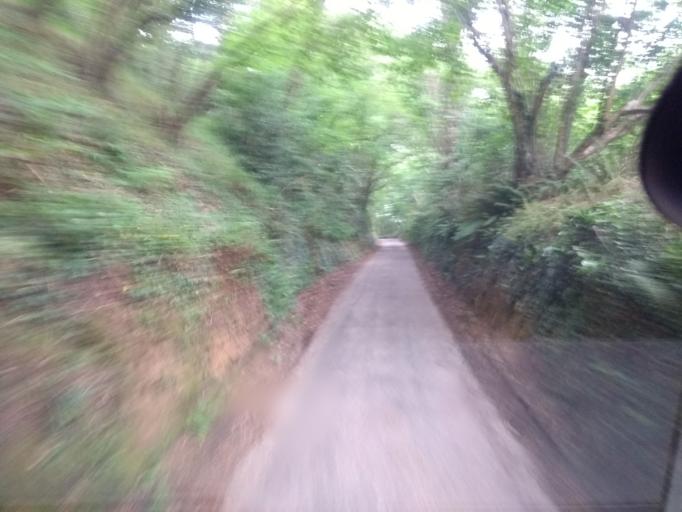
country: GB
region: England
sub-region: Dorset
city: Bridport
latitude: 50.7299
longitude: -2.7910
